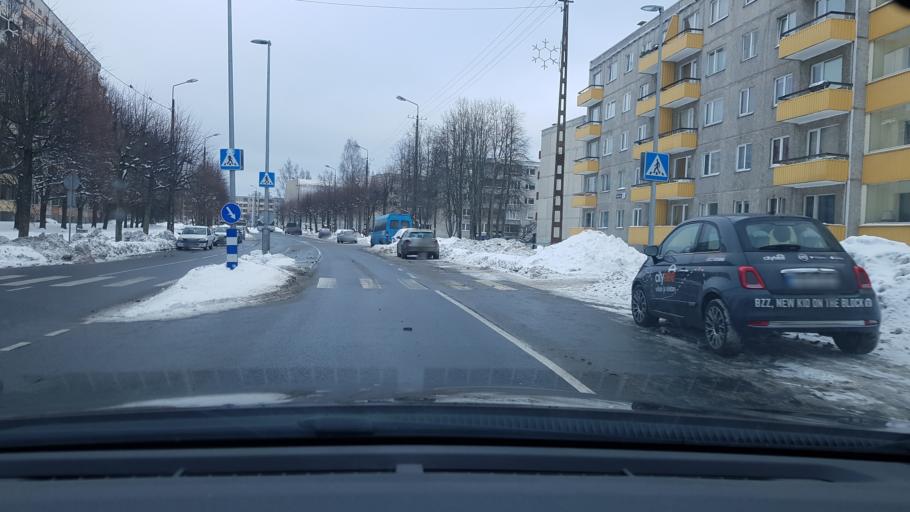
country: EE
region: Harju
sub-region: Saue vald
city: Laagri
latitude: 59.4154
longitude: 24.6397
